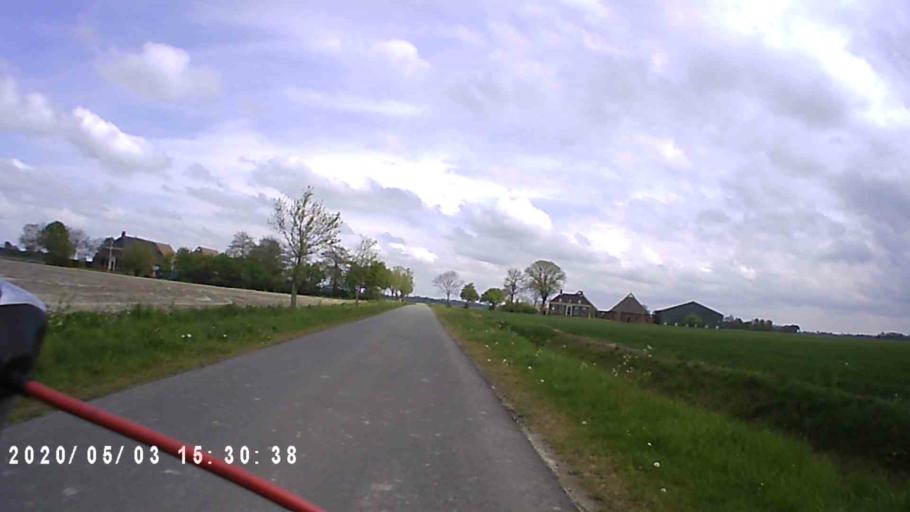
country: NL
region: Groningen
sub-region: Gemeente Winsum
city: Winsum
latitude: 53.3458
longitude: 6.4659
